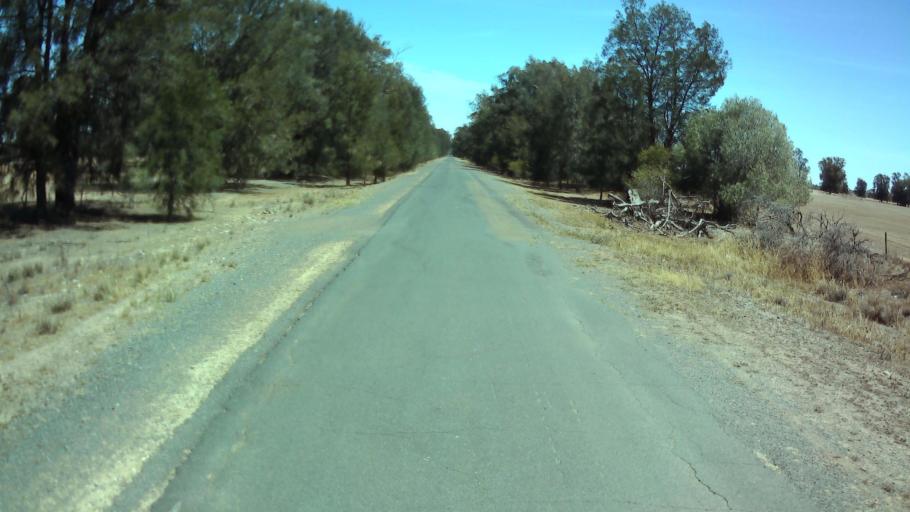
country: AU
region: New South Wales
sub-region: Weddin
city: Grenfell
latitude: -33.8762
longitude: 147.6911
